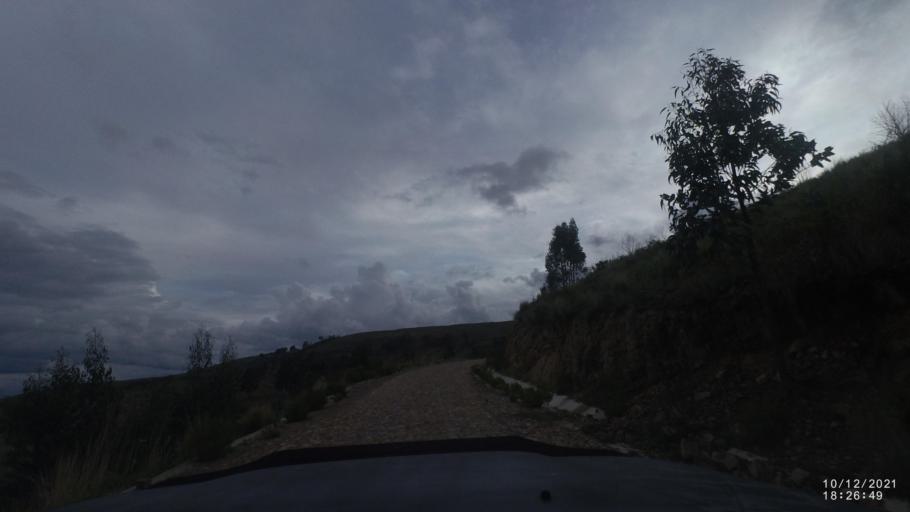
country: BO
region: Cochabamba
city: Tarata
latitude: -17.7991
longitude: -65.9746
